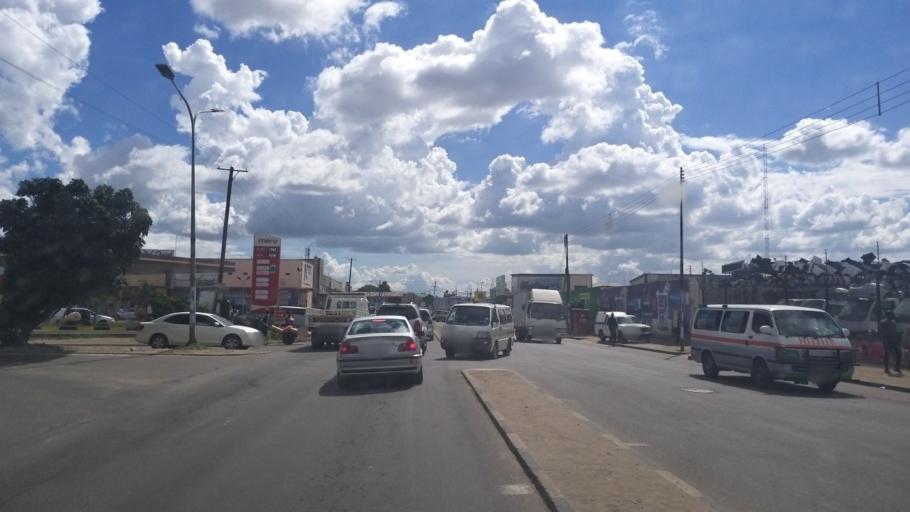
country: ZM
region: Lusaka
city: Lusaka
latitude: -15.4109
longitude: 28.2779
